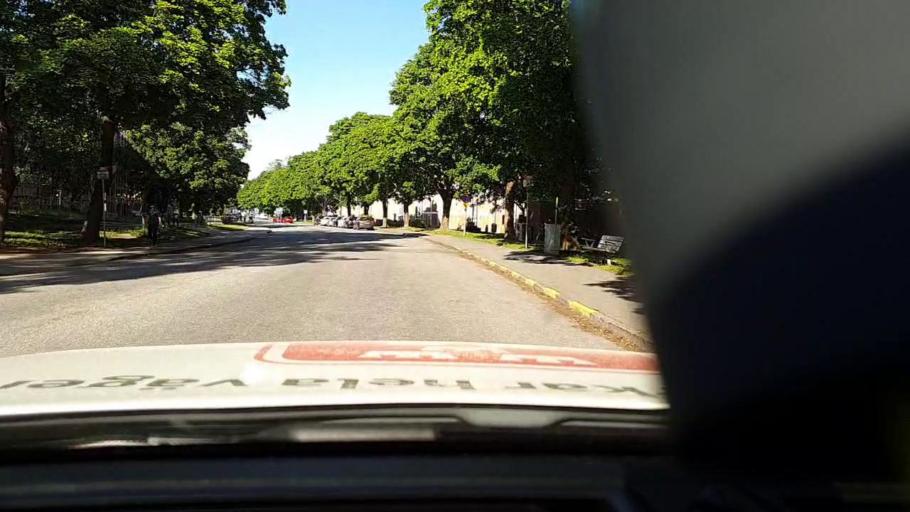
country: SE
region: Stockholm
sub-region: Stockholms Kommun
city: Arsta
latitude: 59.2545
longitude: 18.0751
